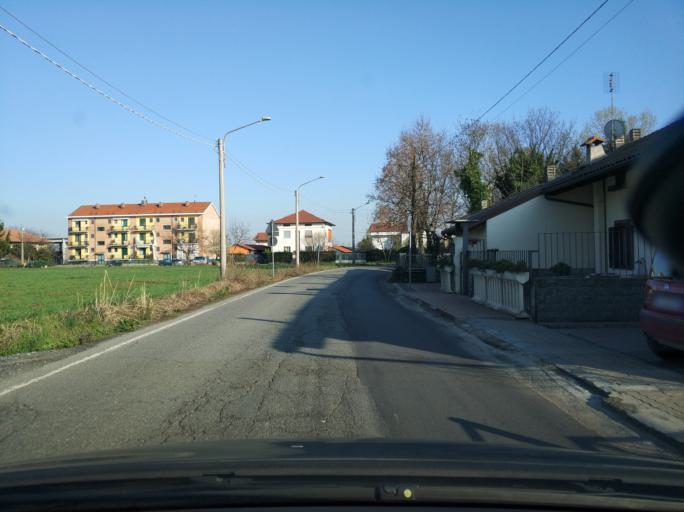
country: IT
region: Piedmont
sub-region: Provincia di Torino
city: Cirie
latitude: 45.2128
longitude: 7.5921
